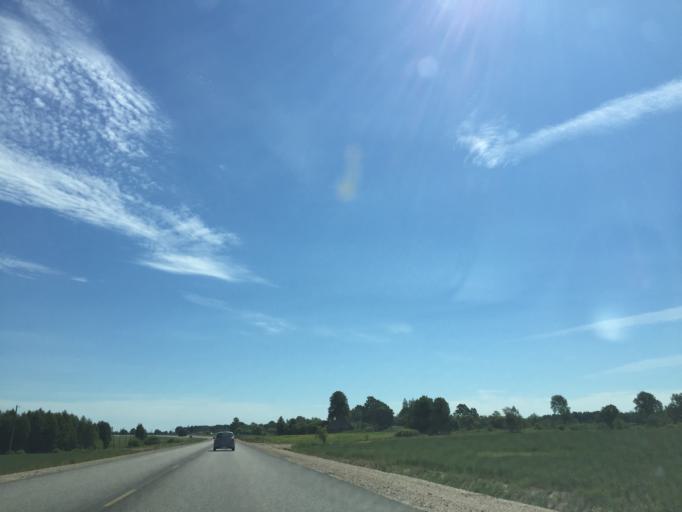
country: LV
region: Saldus Rajons
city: Saldus
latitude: 56.6694
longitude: 22.4071
